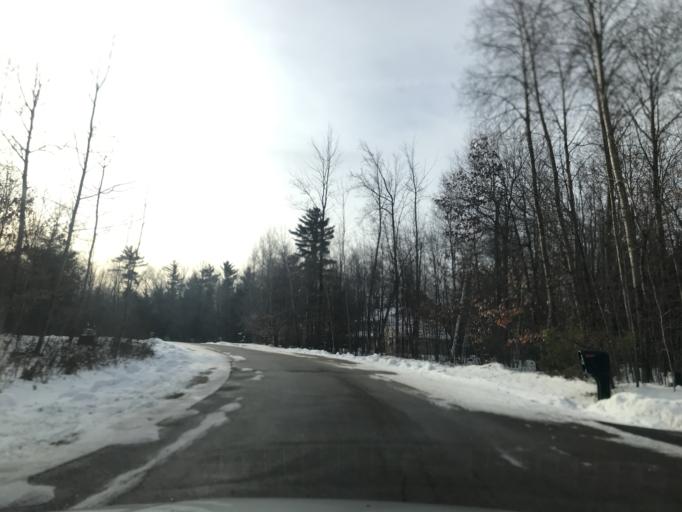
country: US
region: Wisconsin
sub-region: Brown County
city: Suamico
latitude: 44.6890
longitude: -88.0634
